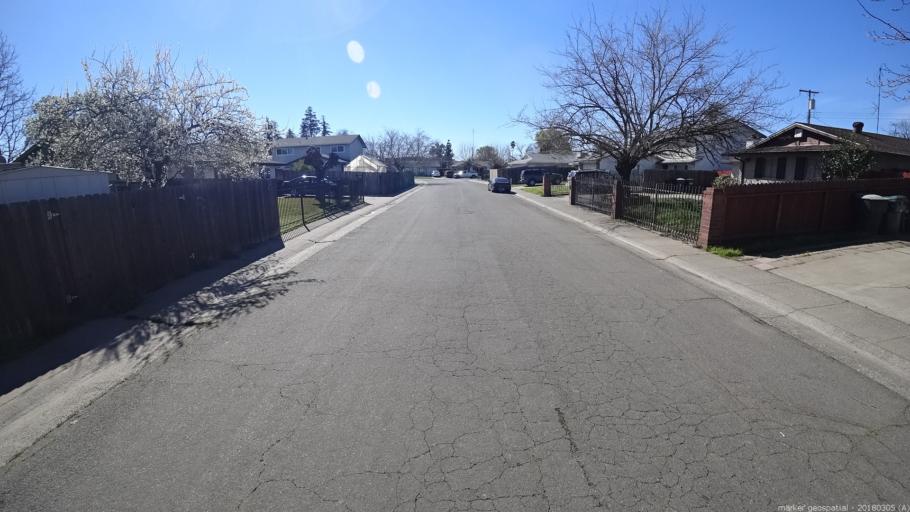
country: US
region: California
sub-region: Sacramento County
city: Florin
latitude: 38.5012
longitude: -121.4182
